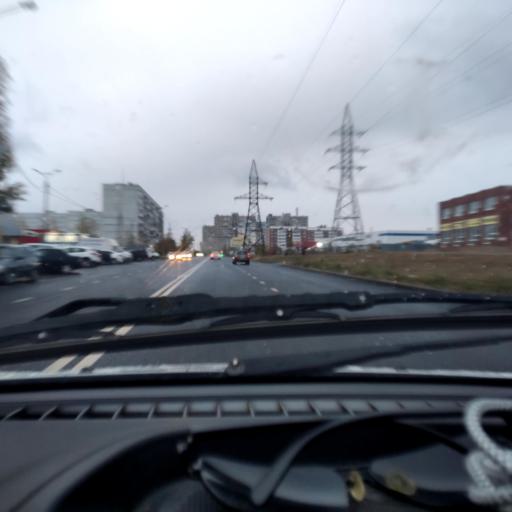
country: RU
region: Samara
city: Zhigulevsk
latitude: 53.4734
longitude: 49.5240
